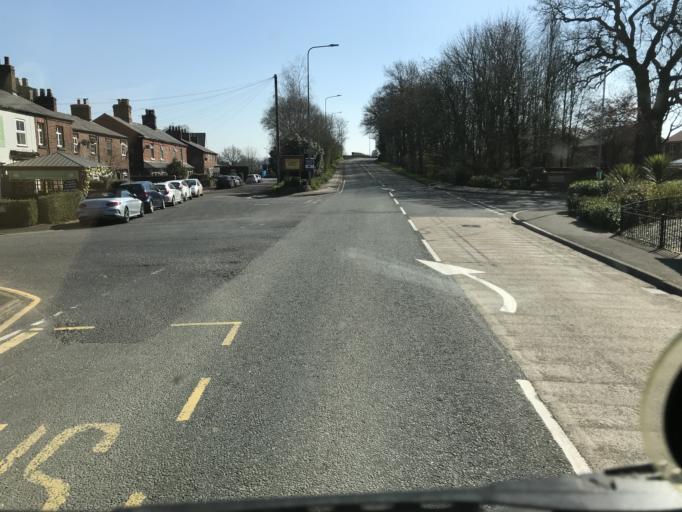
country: GB
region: England
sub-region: Cheshire East
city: Alderley Edge
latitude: 53.2710
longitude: -2.2830
